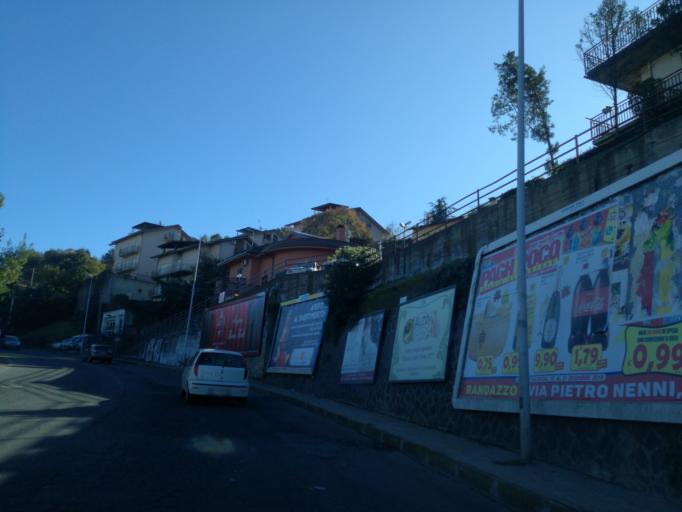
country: IT
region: Sicily
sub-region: Catania
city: Bronte
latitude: 37.7817
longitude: 14.8288
